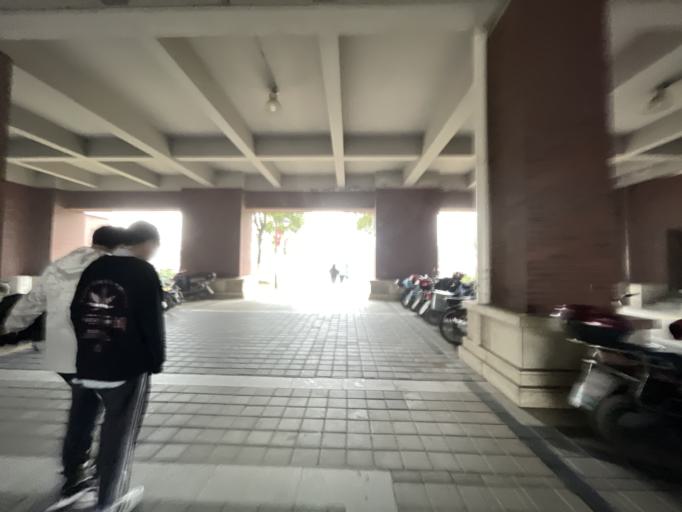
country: CN
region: Shanghai Shi
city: Shuyuan
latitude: 30.8947
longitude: 121.8889
